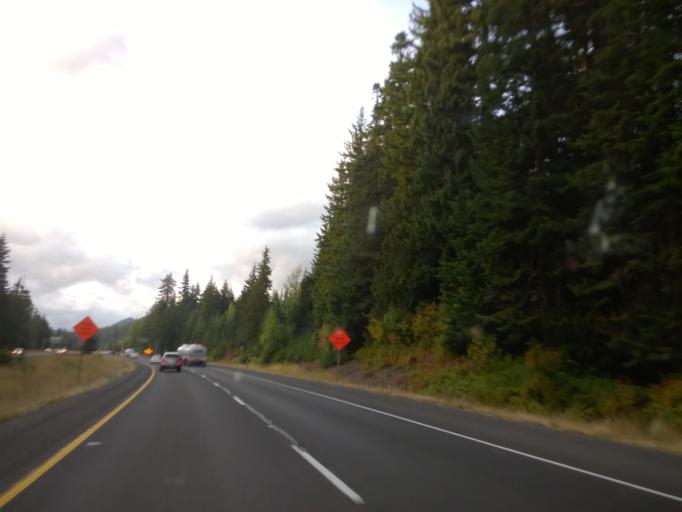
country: US
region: Washington
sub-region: Kittitas County
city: Cle Elum
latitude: 47.3141
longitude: -121.3152
